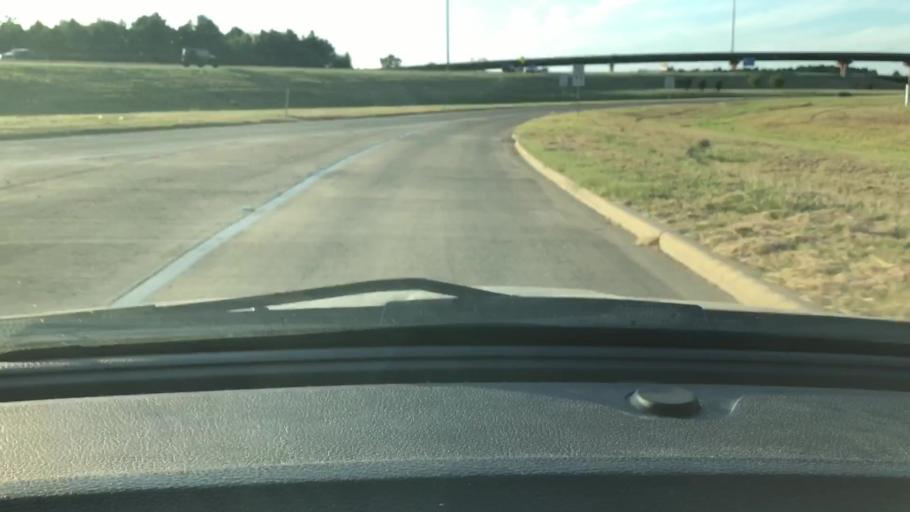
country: US
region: Texas
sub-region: Bowie County
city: Wake Village
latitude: 33.3904
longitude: -94.0965
